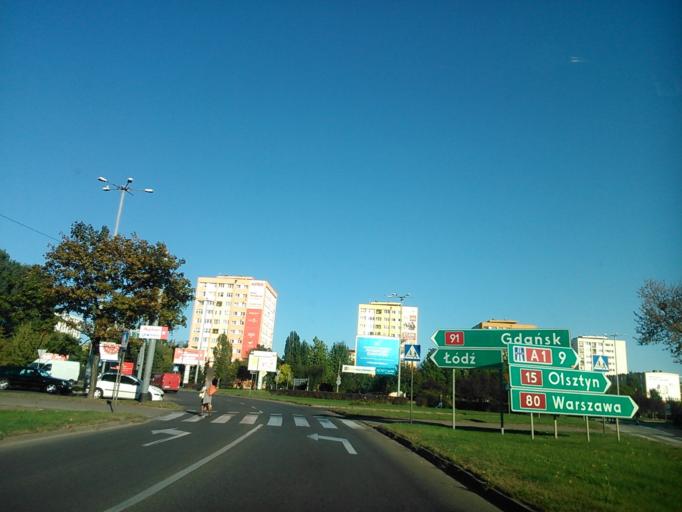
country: PL
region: Kujawsko-Pomorskie
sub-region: Torun
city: Torun
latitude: 53.0178
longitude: 18.6126
